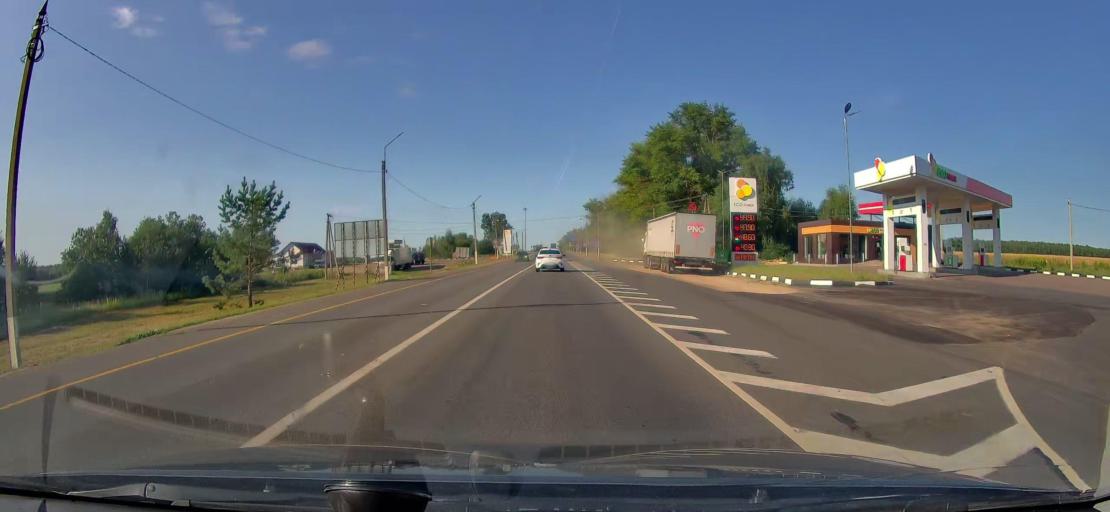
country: RU
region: Orjol
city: Spasskoye-Lutovinovo
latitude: 53.3470
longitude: 36.7117
